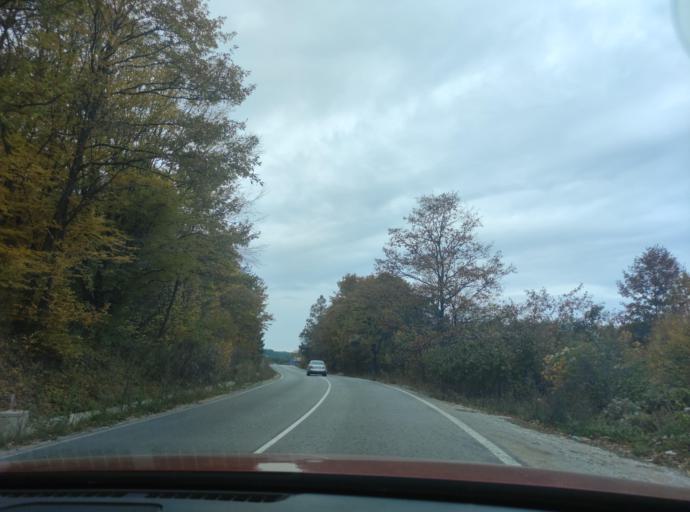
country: BG
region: Sofiya
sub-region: Obshtina Godech
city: Godech
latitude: 42.9805
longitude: 23.1340
